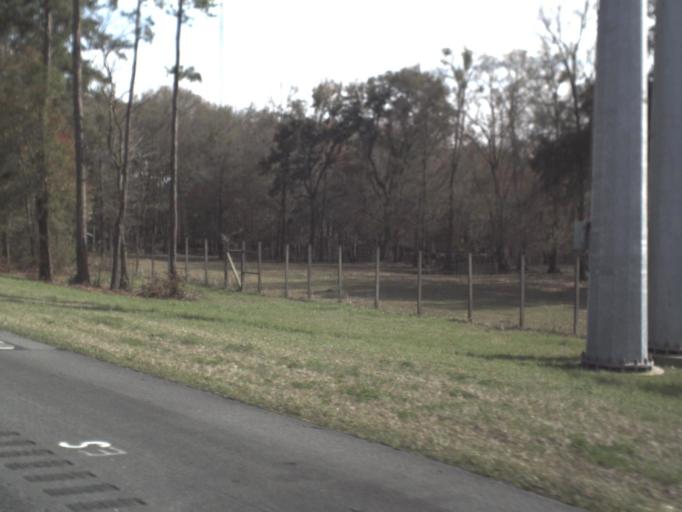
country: US
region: Florida
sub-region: Leon County
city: Tallahassee
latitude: 30.4891
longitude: -84.1646
